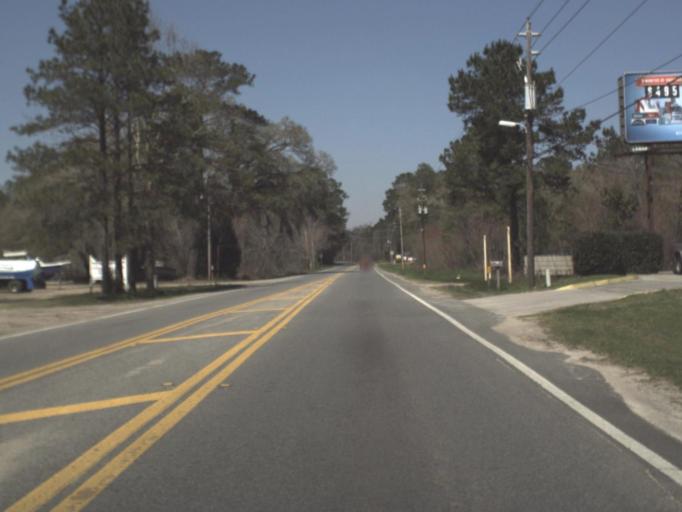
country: US
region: Florida
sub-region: Leon County
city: Woodville
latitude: 30.3284
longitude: -84.2505
